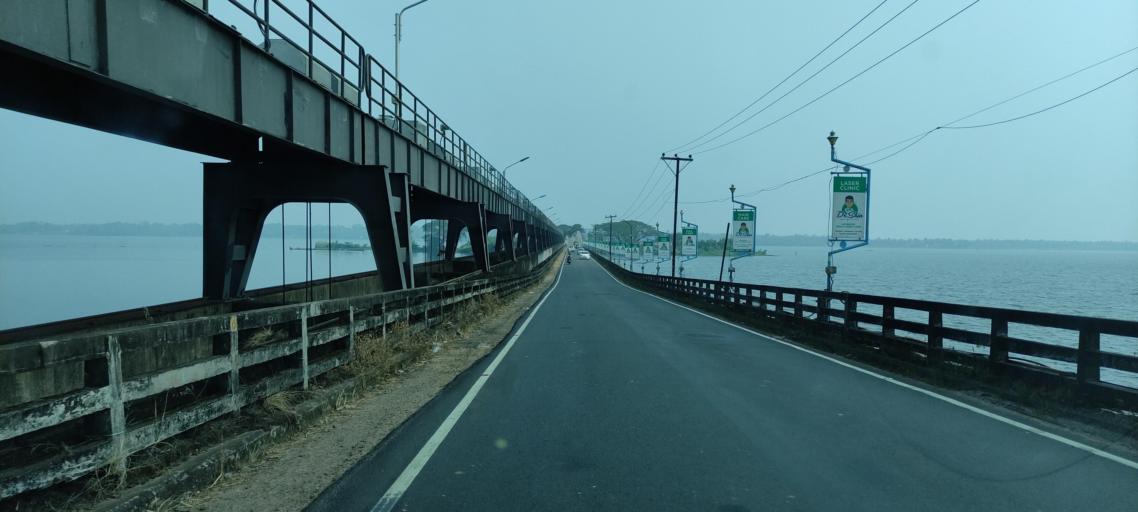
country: IN
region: Kerala
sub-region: Alappuzha
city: Shertallai
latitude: 9.6766
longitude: 76.3957
